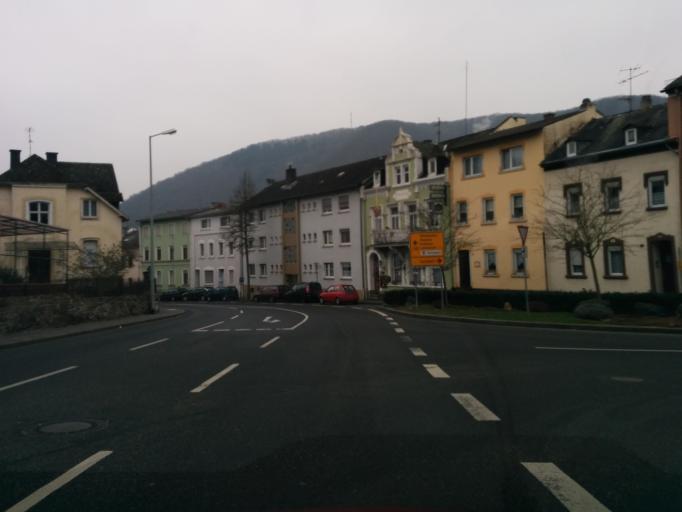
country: DE
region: Rheinland-Pfalz
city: Bad Ems
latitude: 50.3356
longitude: 7.7082
